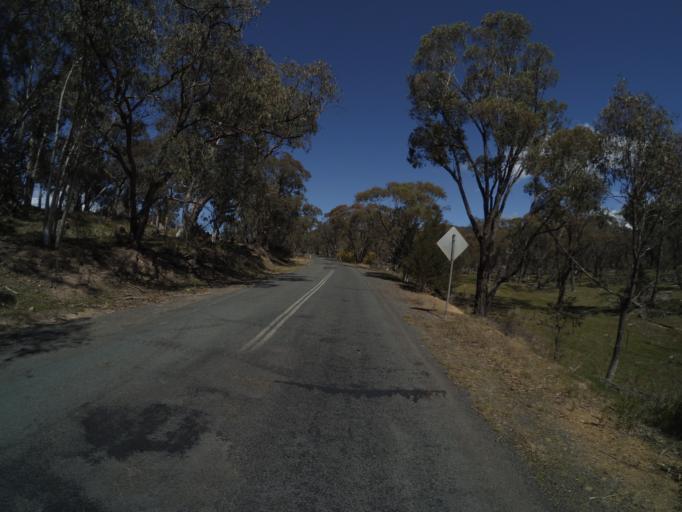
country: AU
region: Australian Capital Territory
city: Macquarie
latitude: -35.2004
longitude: 148.8950
